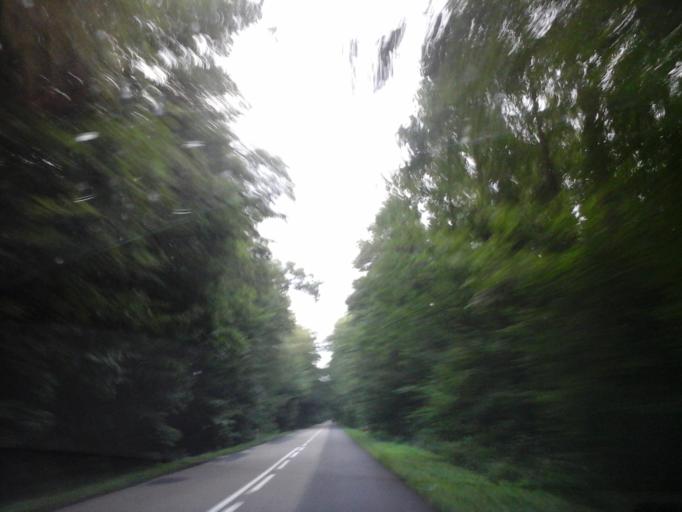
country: PL
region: West Pomeranian Voivodeship
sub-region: Powiat kamienski
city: Golczewo
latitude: 53.7818
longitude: 15.0212
